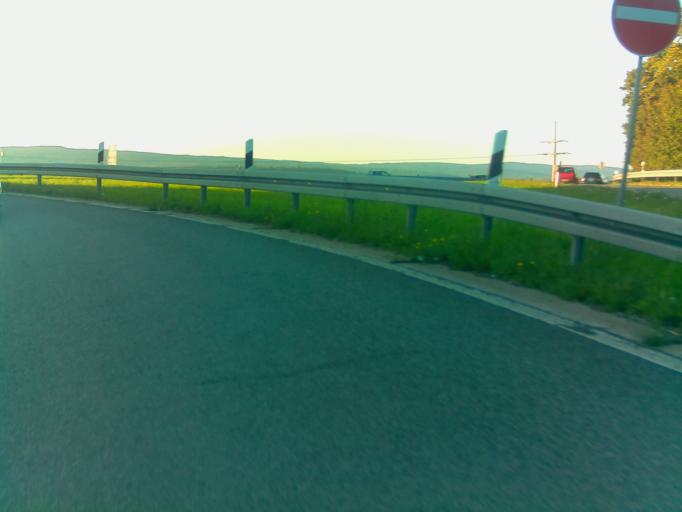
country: DE
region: Hesse
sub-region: Regierungsbezirk Darmstadt
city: Bad Homburg vor der Hoehe
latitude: 50.2012
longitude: 8.6477
